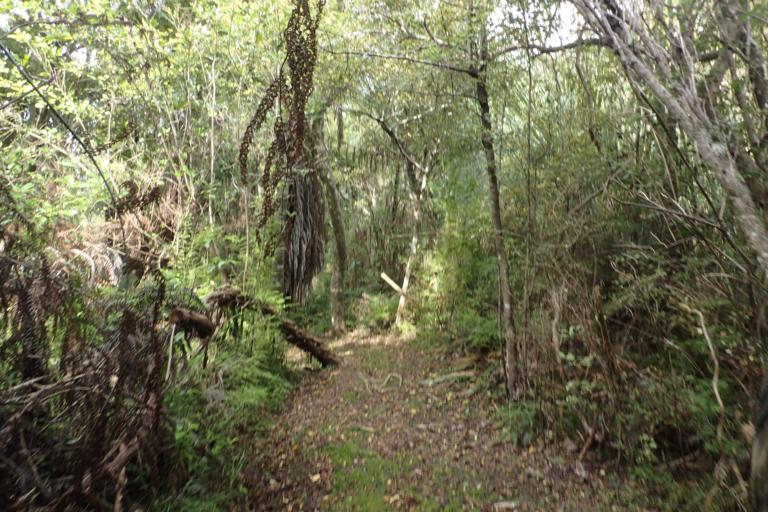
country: NZ
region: Auckland
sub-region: Auckland
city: Pakuranga
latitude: -36.7881
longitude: 175.0055
